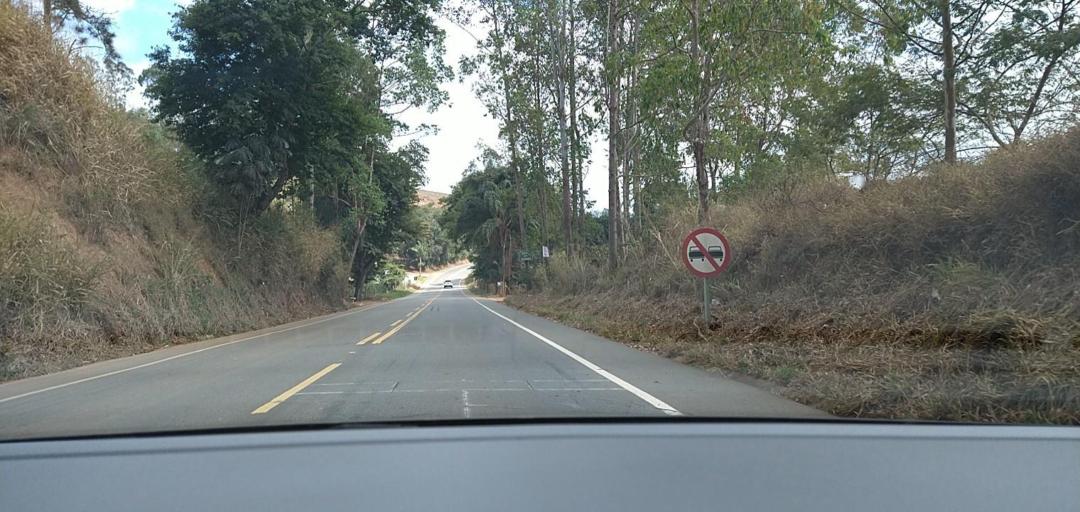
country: BR
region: Minas Gerais
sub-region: Vicosa
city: Vicosa
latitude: -20.6037
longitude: -42.8692
